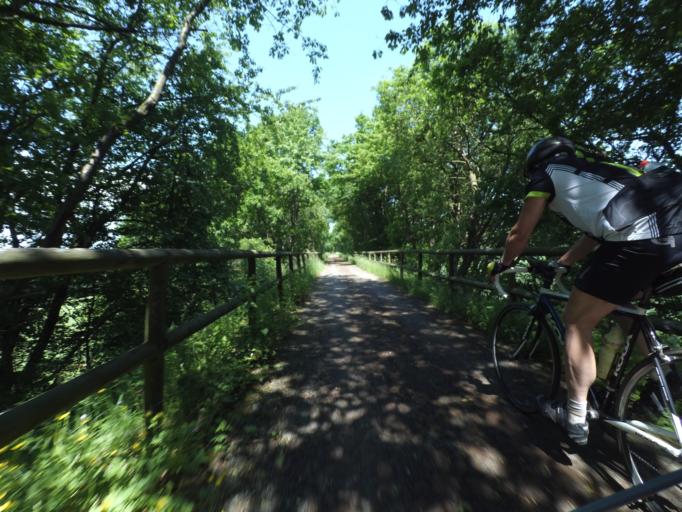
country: DE
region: Rheinland-Pfalz
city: Leiningen
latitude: 50.1220
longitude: 7.5700
